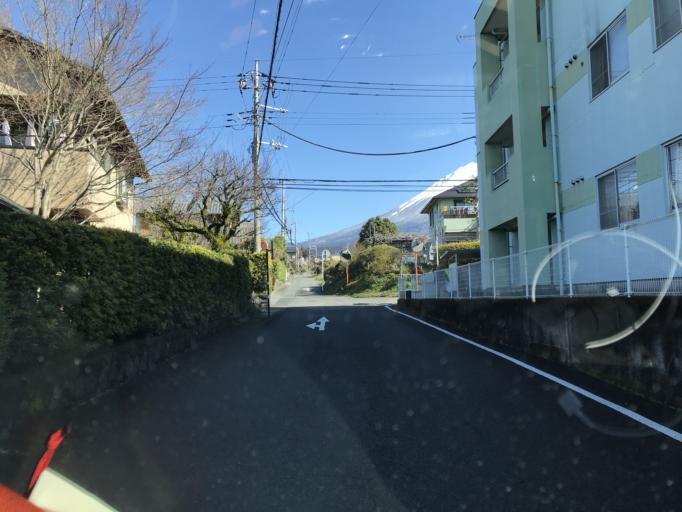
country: JP
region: Shizuoka
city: Fujinomiya
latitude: 35.2557
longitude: 138.6301
